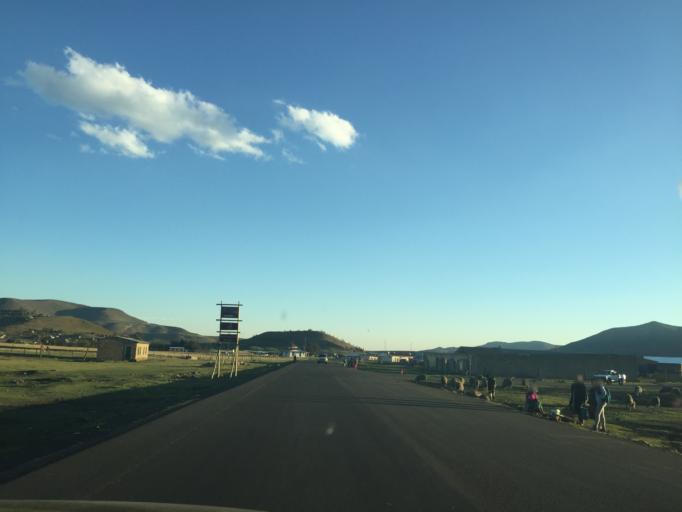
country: LS
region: Maseru
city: Nako
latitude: -29.8372
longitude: 28.0527
